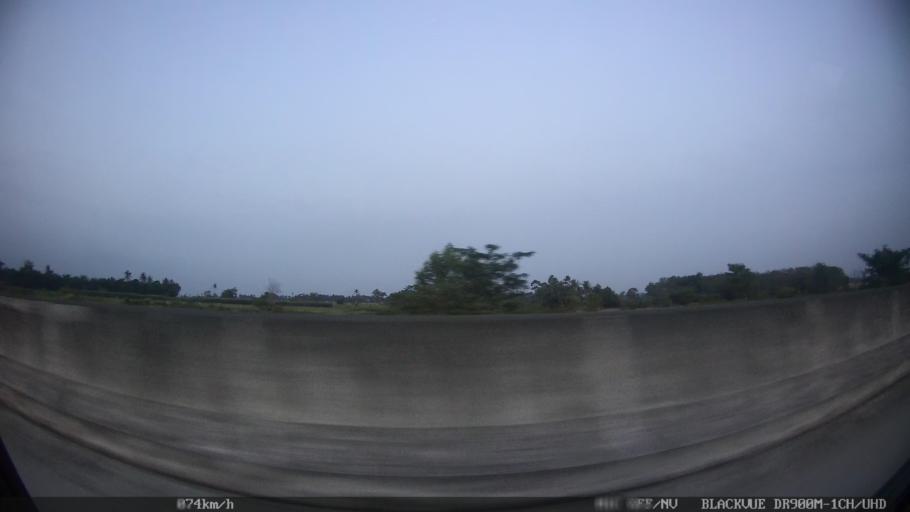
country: ID
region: Lampung
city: Sidorejo
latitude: -5.6263
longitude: 105.5650
